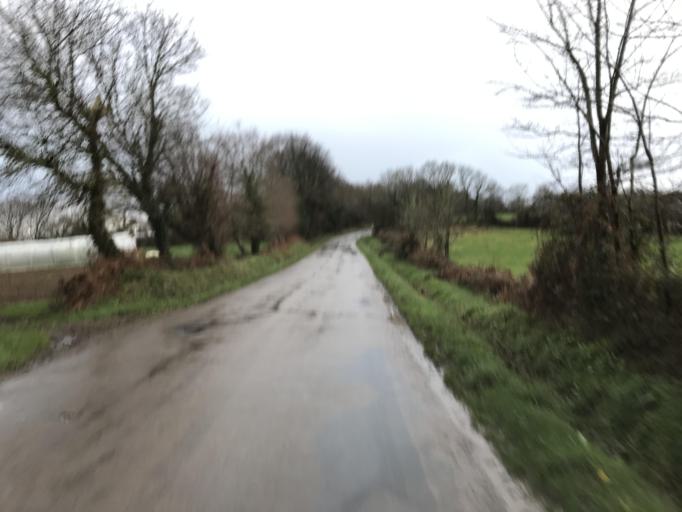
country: FR
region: Brittany
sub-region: Departement du Finistere
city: Loperhet
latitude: 48.3652
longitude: -4.3247
